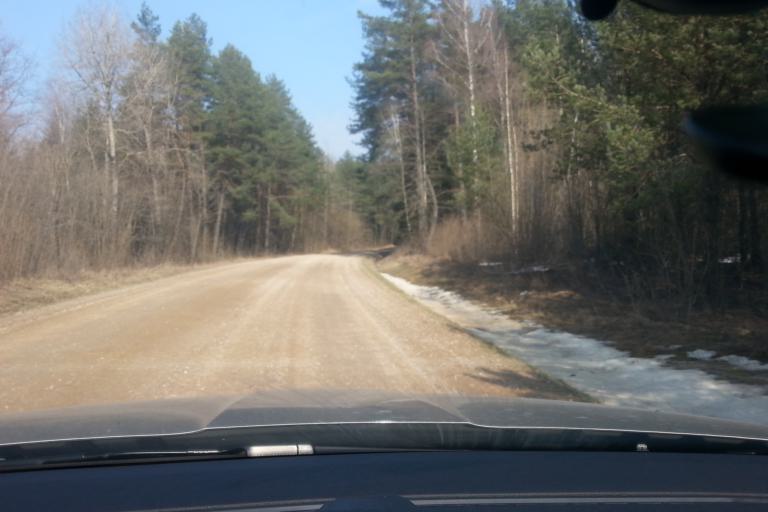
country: LT
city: Trakai
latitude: 54.5749
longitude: 24.9682
